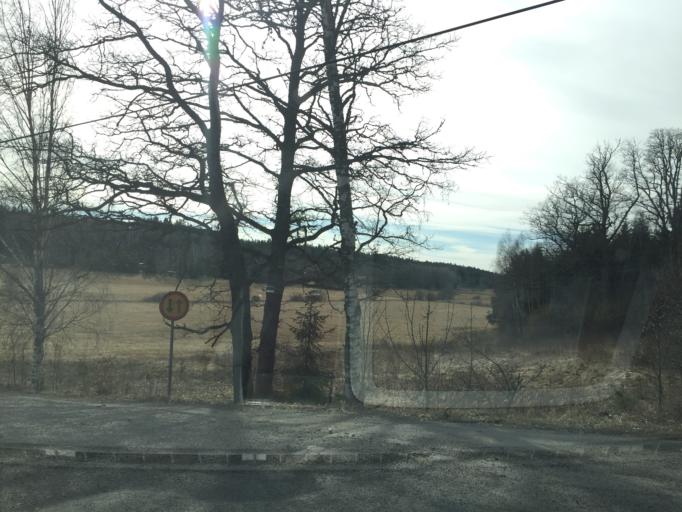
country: SE
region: Stockholm
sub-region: Botkyrka Kommun
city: Tullinge
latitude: 59.1019
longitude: 17.9659
